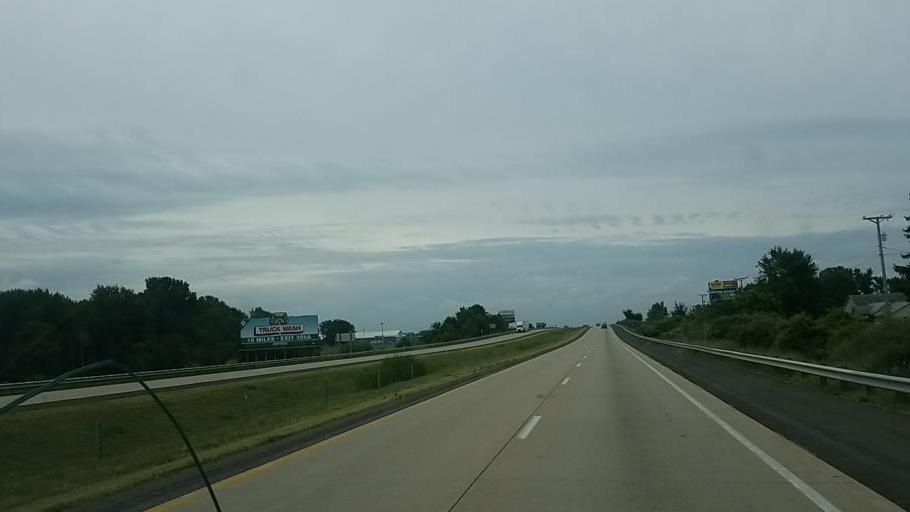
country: US
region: Indiana
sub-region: DeKalb County
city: Auburn
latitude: 41.3403
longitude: -85.0880
